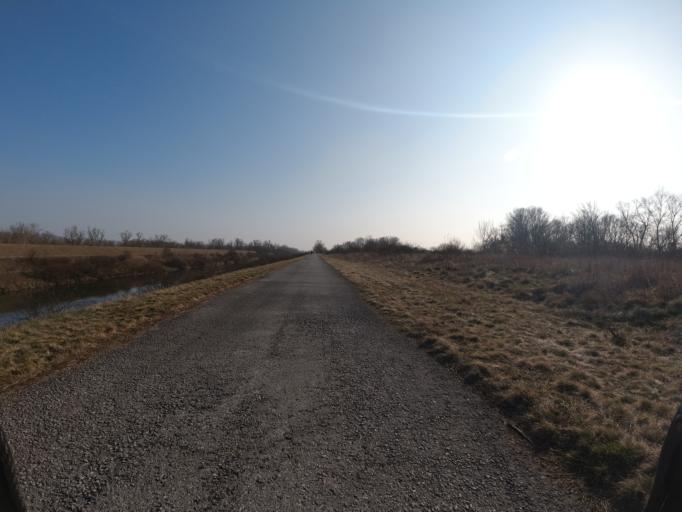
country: SK
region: Trnavsky
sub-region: Okres Trnava
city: Piestany
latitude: 48.6331
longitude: 17.8430
